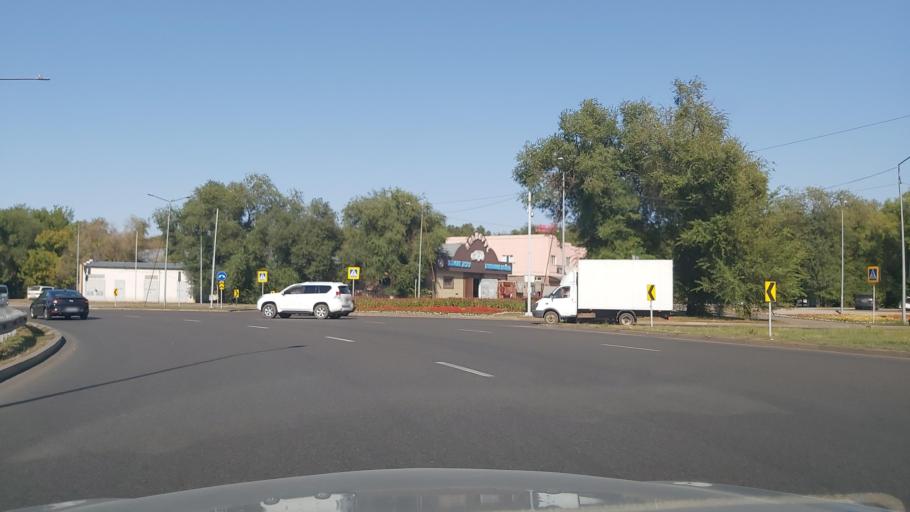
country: KZ
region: Almaty Qalasy
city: Almaty
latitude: 43.3026
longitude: 76.8963
